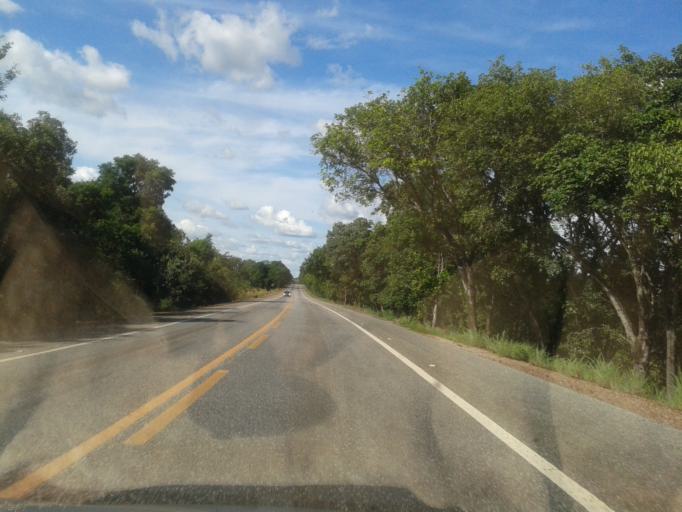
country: BR
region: Goias
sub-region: Mozarlandia
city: Mozarlandia
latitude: -14.8617
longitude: -50.5470
